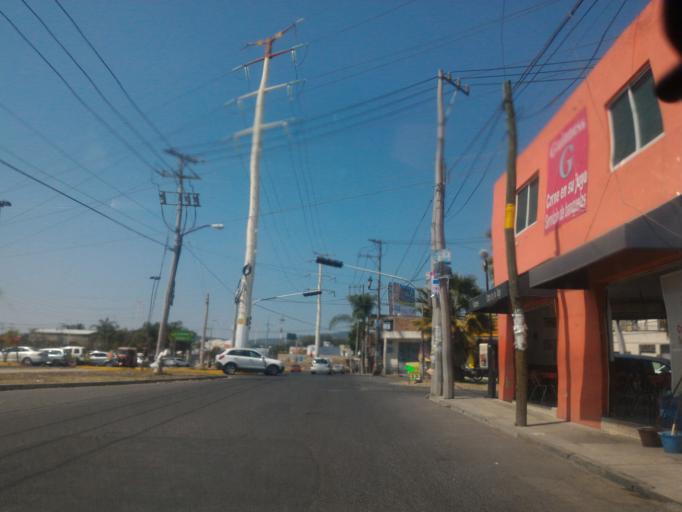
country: MX
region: Jalisco
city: Santa Anita
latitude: 20.5556
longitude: -103.4524
